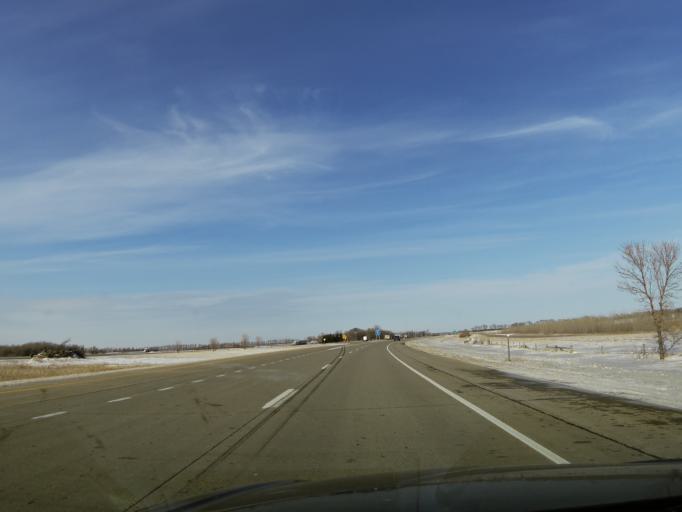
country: US
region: North Dakota
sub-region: Walsh County
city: Grafton
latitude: 48.4544
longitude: -97.1943
